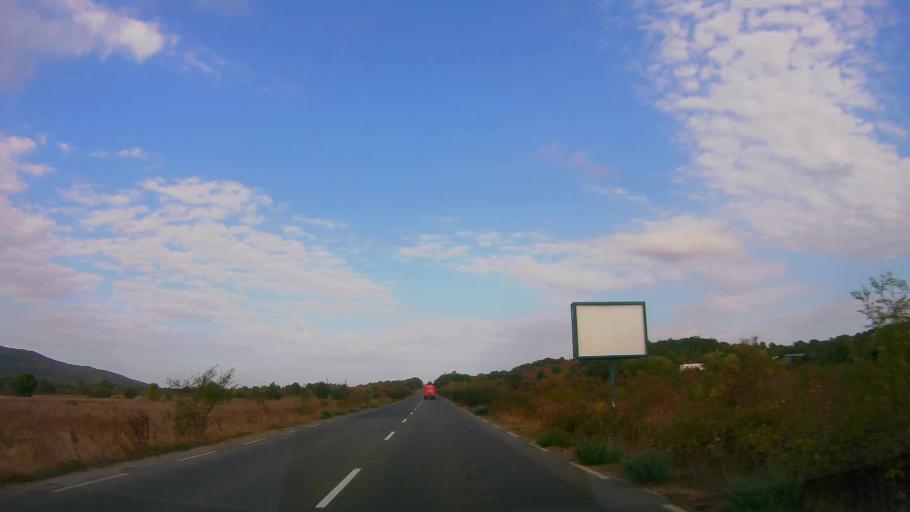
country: BG
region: Burgas
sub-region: Obshtina Sozopol
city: Sozopol
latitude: 42.3660
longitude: 27.6918
